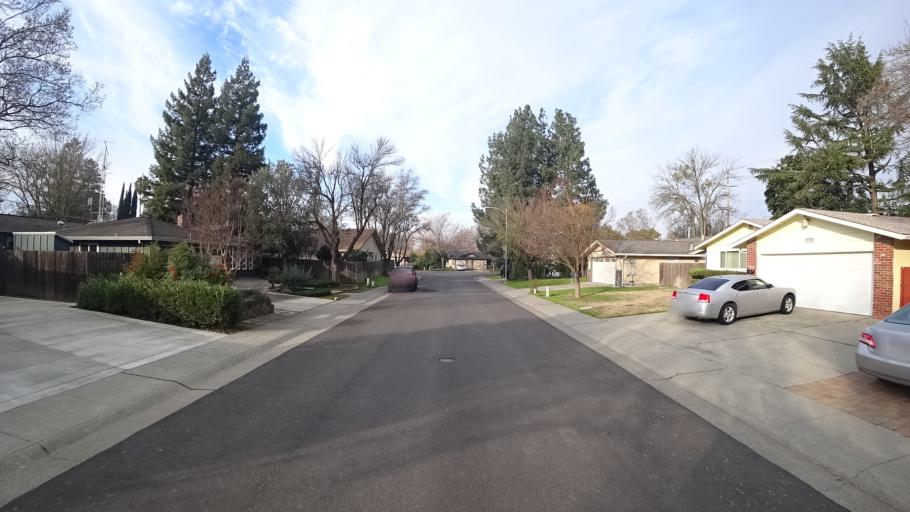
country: US
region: California
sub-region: Yolo County
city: Davis
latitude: 38.5633
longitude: -121.7138
